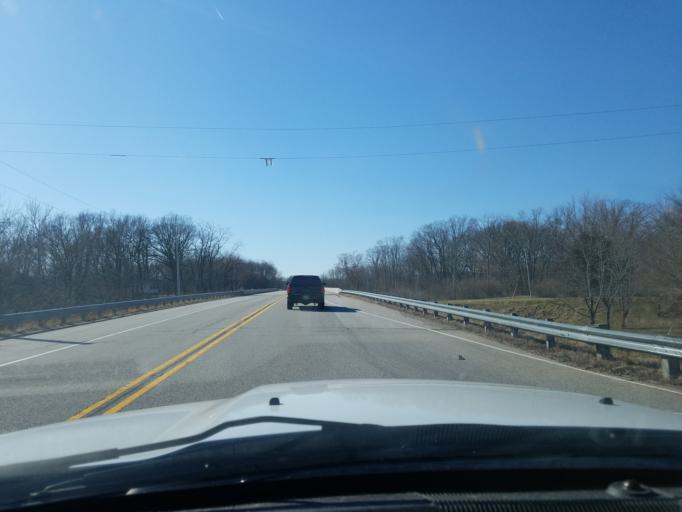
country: US
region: Indiana
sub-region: Johnson County
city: Franklin
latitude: 39.4953
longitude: -85.9473
